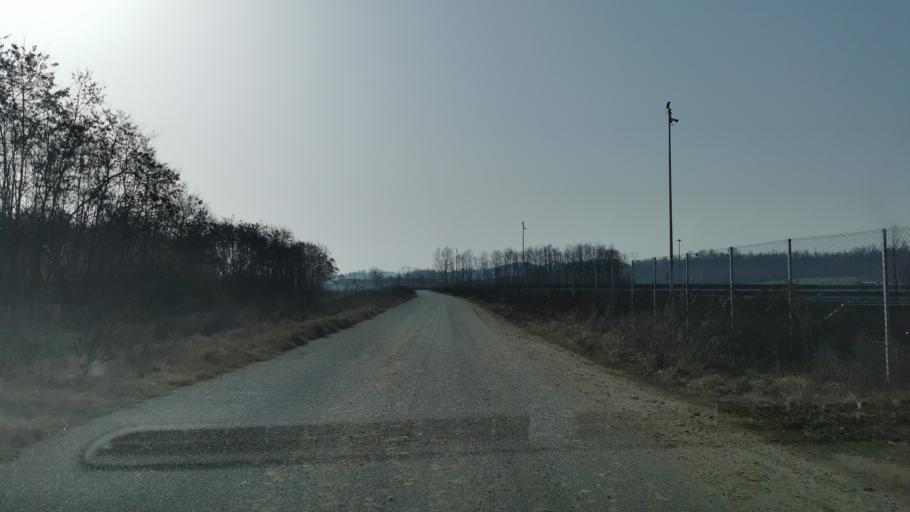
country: IT
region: Piedmont
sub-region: Provincia di Torino
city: Lombardore
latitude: 45.2313
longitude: 7.7554
